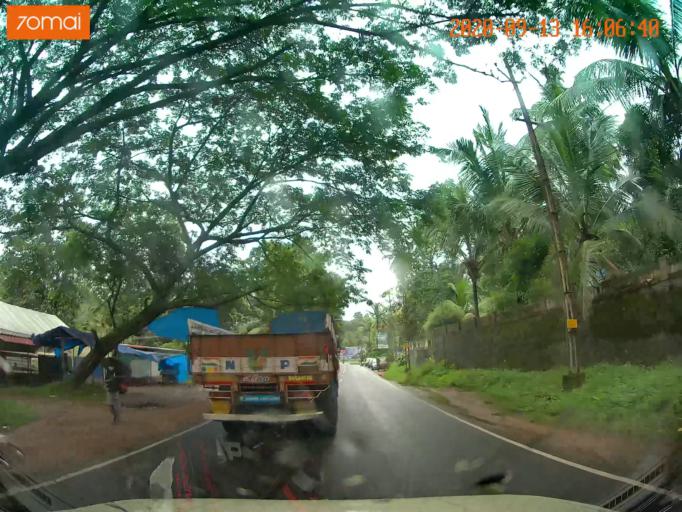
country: IN
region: Kerala
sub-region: Kottayam
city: Palackattumala
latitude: 9.6721
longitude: 76.5823
